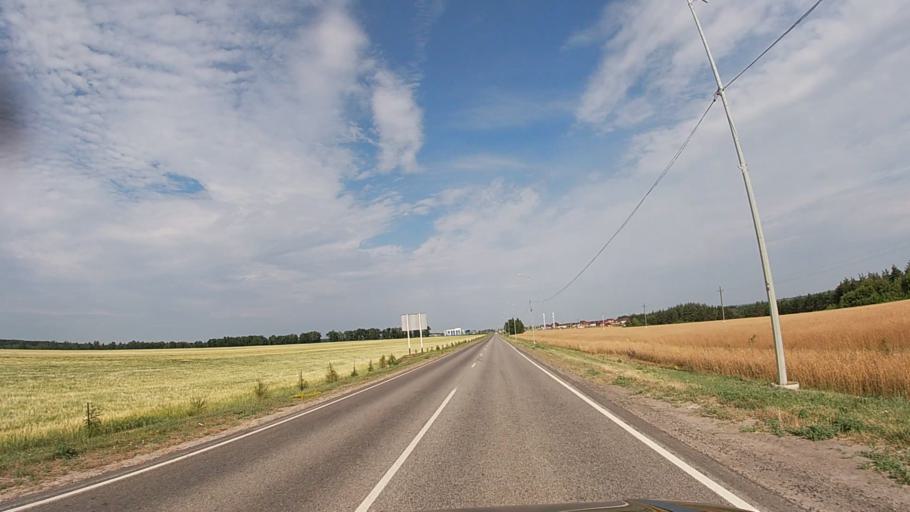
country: RU
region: Belgorod
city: Krasnaya Yaruga
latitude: 50.7962
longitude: 35.7057
